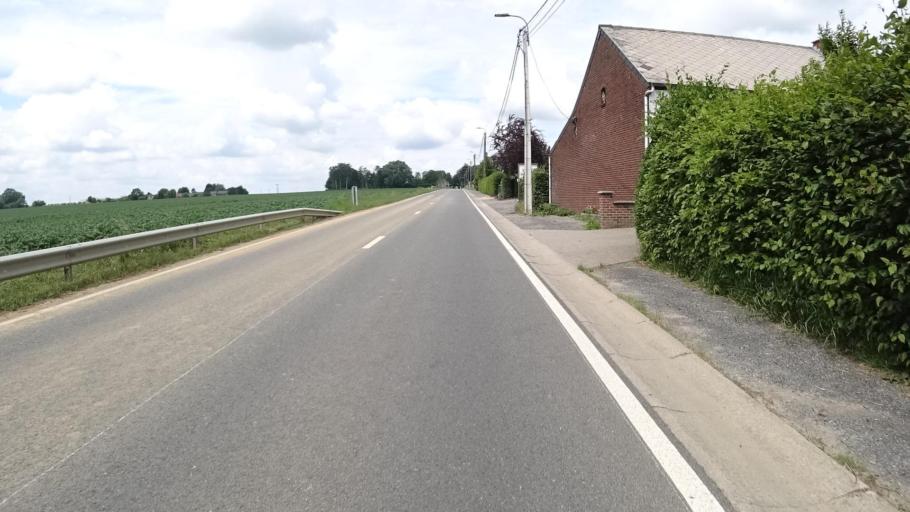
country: BE
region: Wallonia
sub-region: Province de Namur
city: Namur
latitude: 50.5378
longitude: 4.8423
